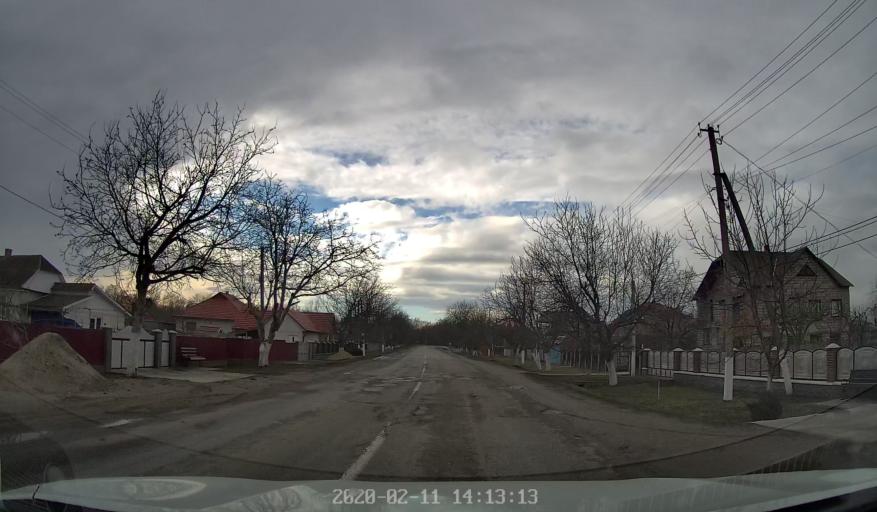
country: RO
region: Botosani
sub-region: Comuna Hudesti
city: Alba
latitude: 48.2208
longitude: 26.4767
